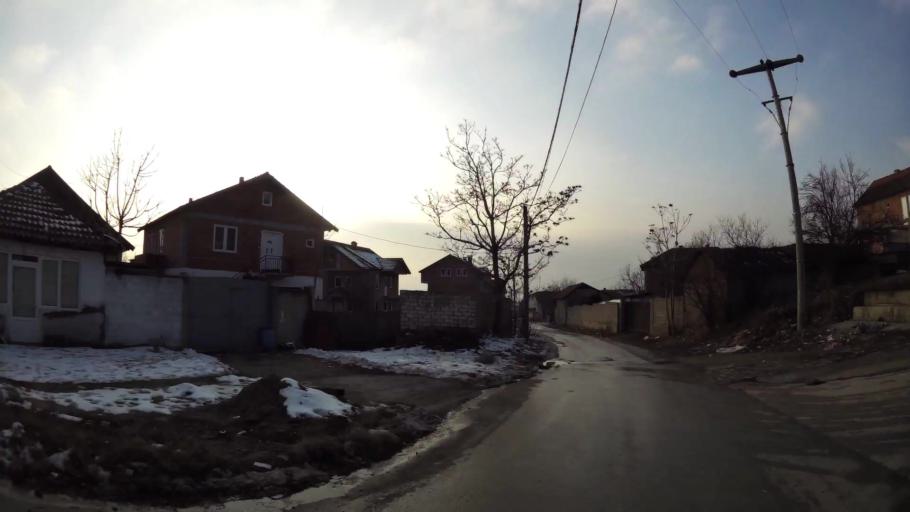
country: MK
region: Aracinovo
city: Arachinovo
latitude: 42.0228
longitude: 21.5675
